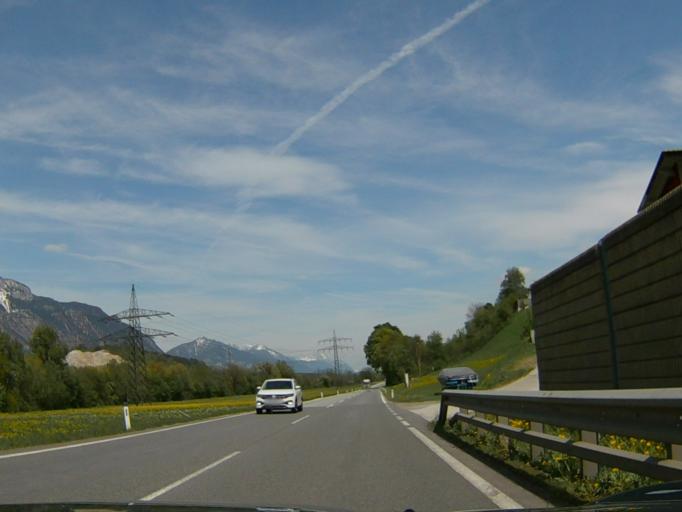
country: AT
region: Tyrol
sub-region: Politischer Bezirk Schwaz
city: Jenbach
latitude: 47.3845
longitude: 11.7826
